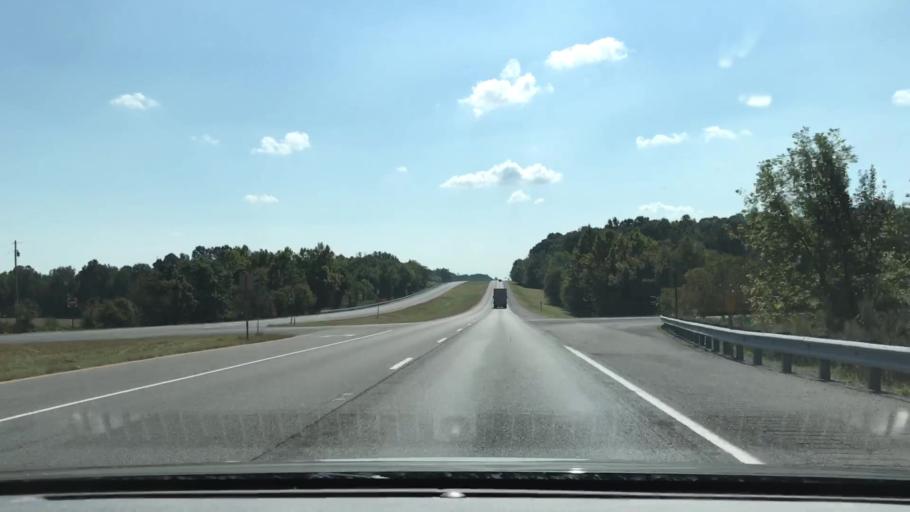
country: US
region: Kentucky
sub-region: Marshall County
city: Benton
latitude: 36.7754
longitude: -88.3195
